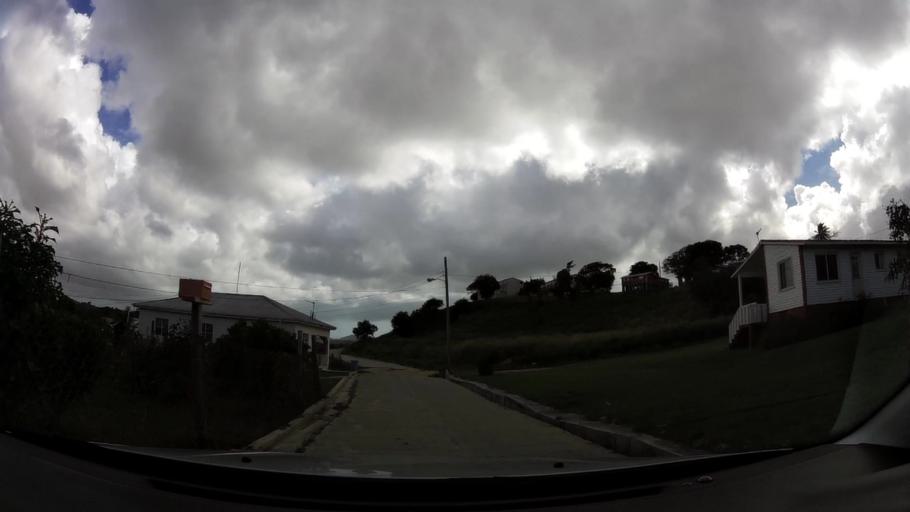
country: AG
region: Saint John
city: Saint John's
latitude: 17.1017
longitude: -61.8391
